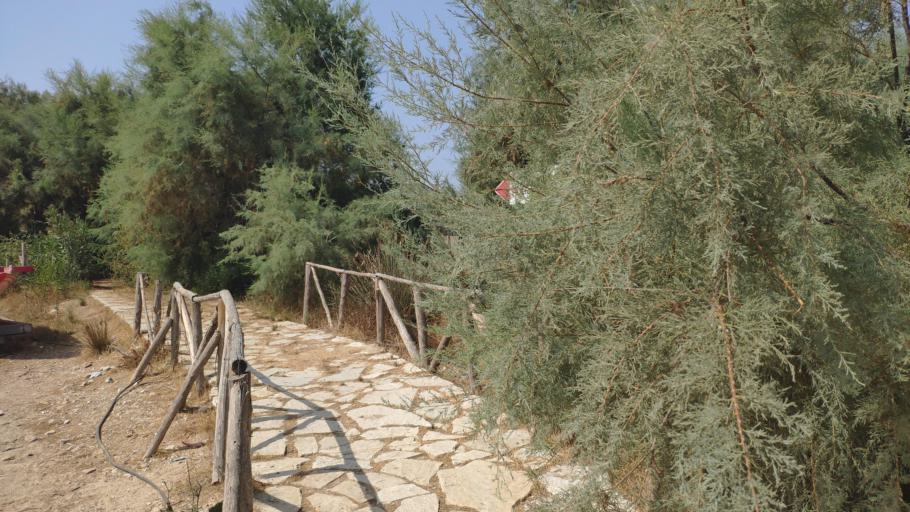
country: GR
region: West Greece
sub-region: Nomos Aitolias kai Akarnanias
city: Menidi
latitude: 39.0382
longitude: 21.0744
